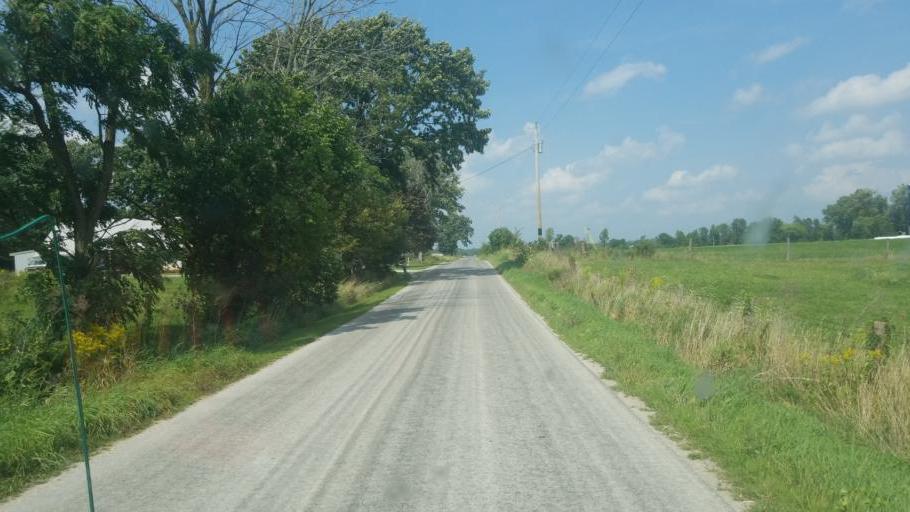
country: US
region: Ohio
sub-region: Huron County
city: Greenwich
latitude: 40.9635
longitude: -82.4316
